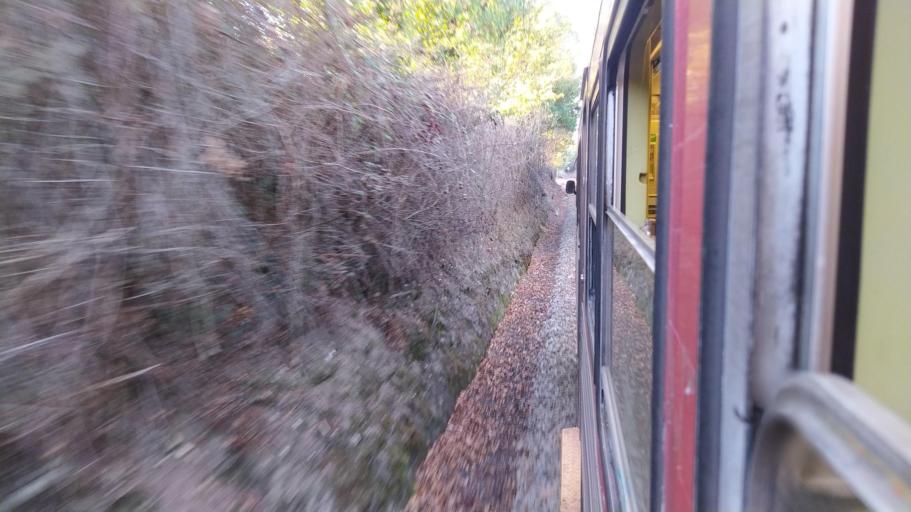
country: PT
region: Aveiro
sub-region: Aveiro
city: Eixo
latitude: 40.6335
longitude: -8.5745
